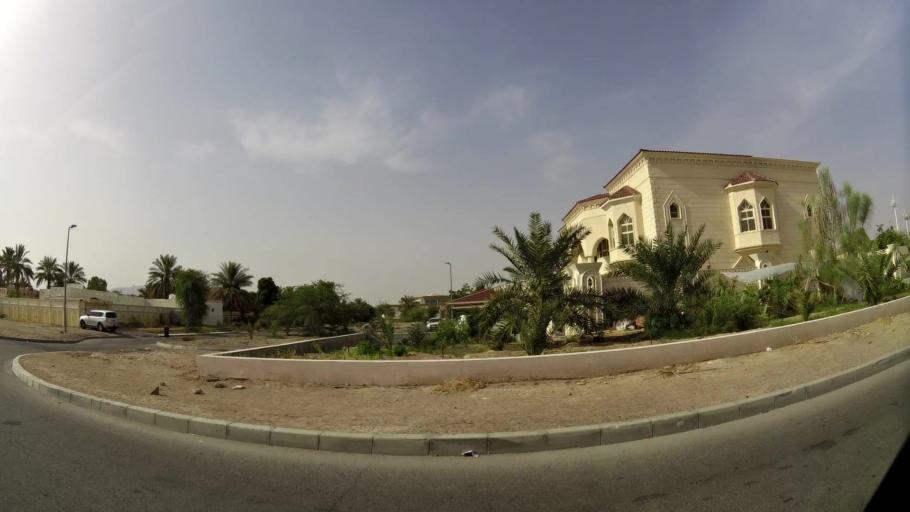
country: AE
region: Abu Dhabi
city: Al Ain
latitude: 24.1385
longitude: 55.7091
